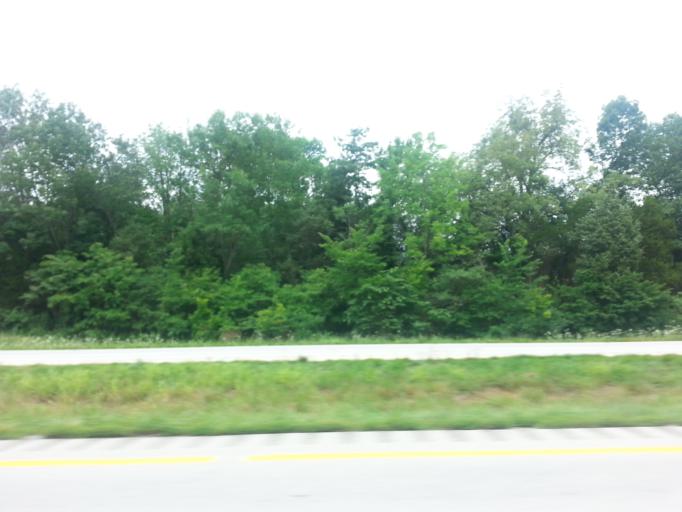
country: US
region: Kentucky
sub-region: Hardin County
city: Elizabethtown
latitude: 37.5800
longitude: -86.0164
